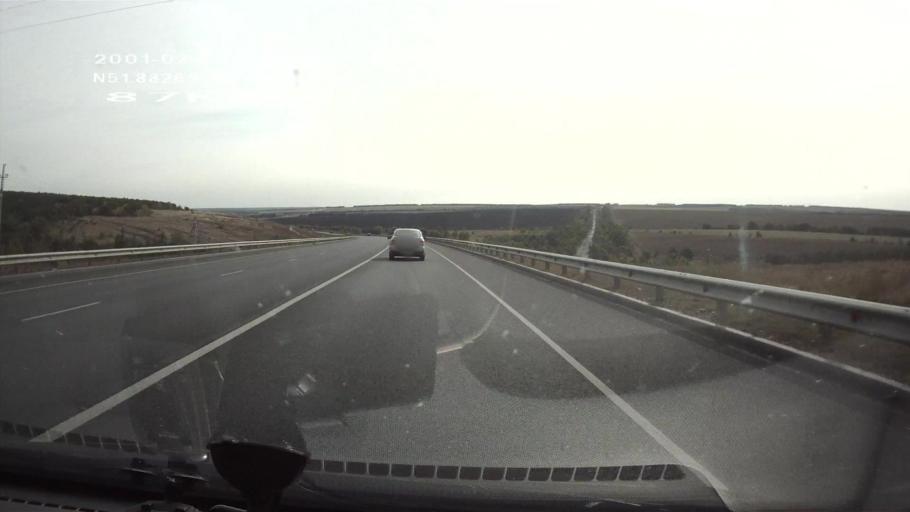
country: RU
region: Saratov
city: Yelshanka
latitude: 51.8824
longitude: 46.5118
